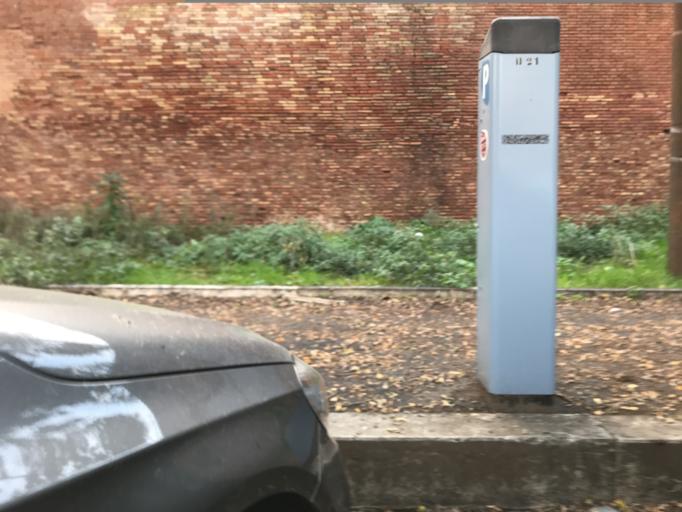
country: IT
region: Latium
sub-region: Citta metropolitana di Roma Capitale
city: Rome
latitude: 41.8994
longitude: 12.5095
